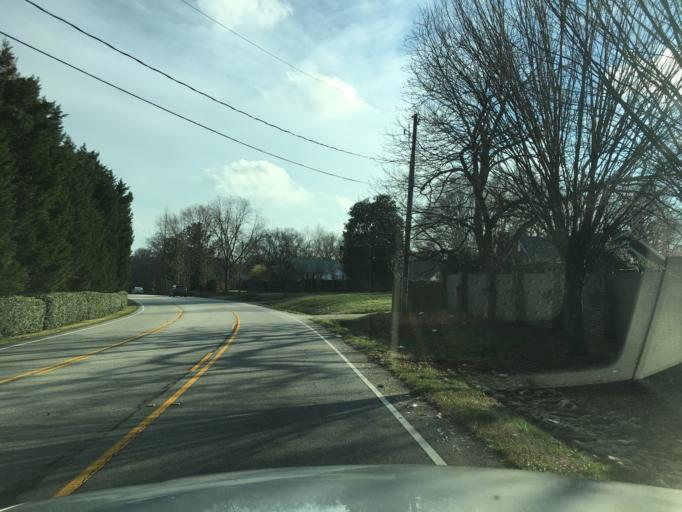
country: US
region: South Carolina
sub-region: Greenville County
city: Taylors
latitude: 34.8892
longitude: -82.2905
